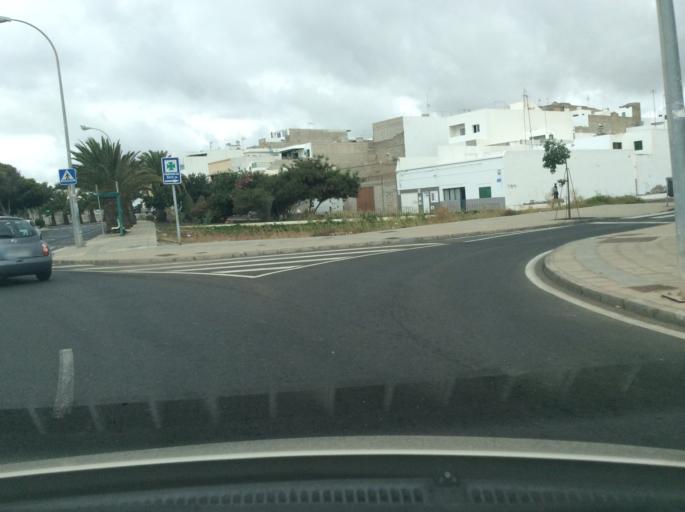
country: ES
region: Canary Islands
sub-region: Provincia de Las Palmas
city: Arrecife
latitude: 28.9675
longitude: -13.5481
